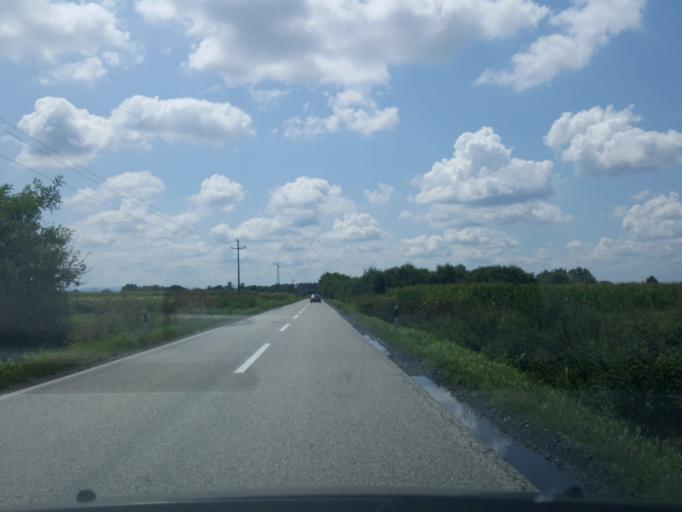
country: RS
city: Metkovic
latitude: 44.8681
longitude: 19.5470
